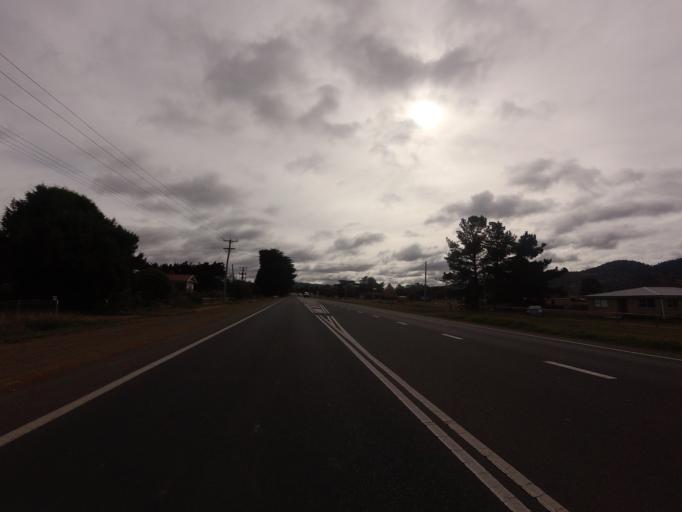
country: AU
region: Tasmania
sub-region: Brighton
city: Bridgewater
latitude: -42.6531
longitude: 147.2406
